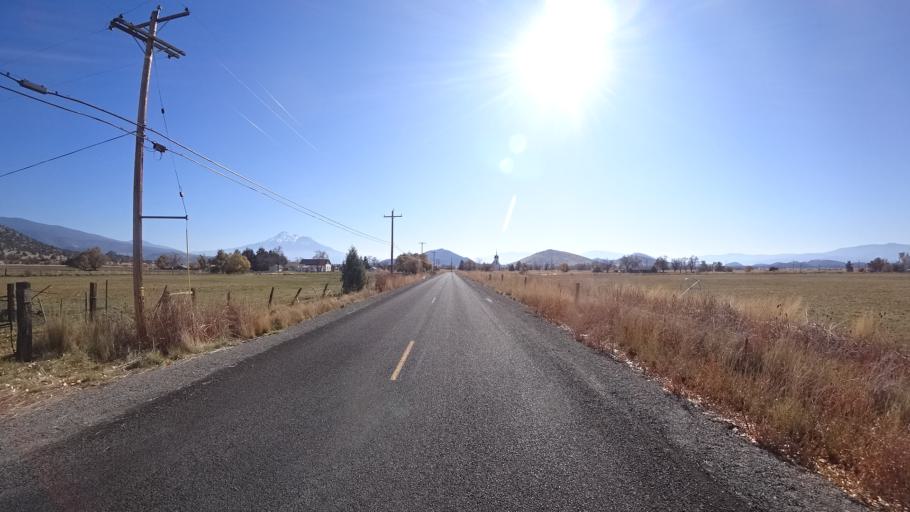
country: US
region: California
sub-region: Siskiyou County
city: Montague
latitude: 41.7144
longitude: -122.3892
